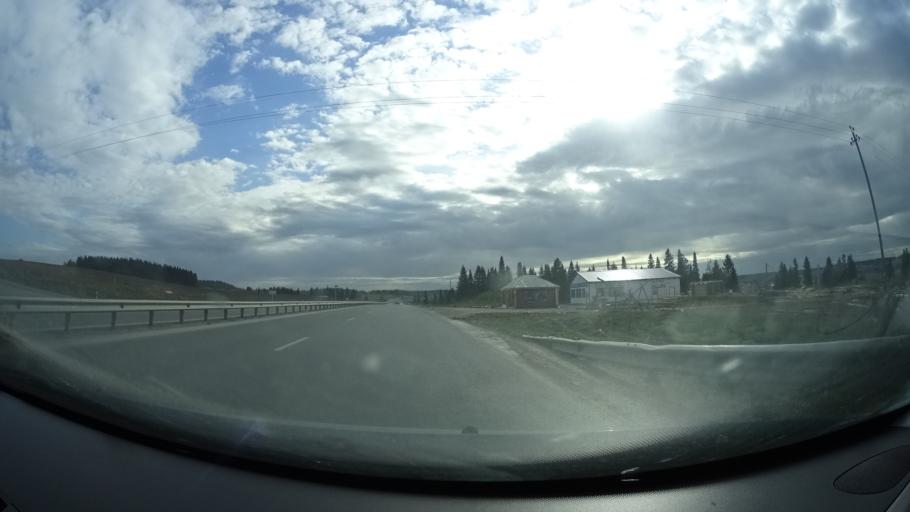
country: RU
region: Perm
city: Kultayevo
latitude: 57.8673
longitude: 55.8857
